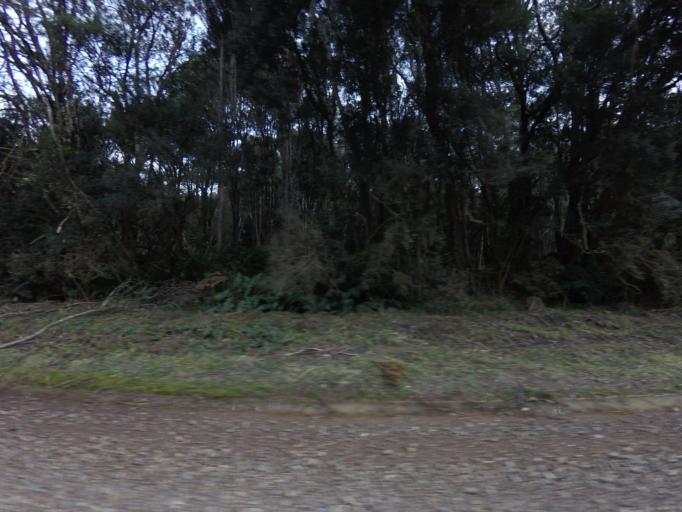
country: AU
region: Tasmania
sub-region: Huon Valley
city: Geeveston
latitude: -43.5433
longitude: 146.8909
